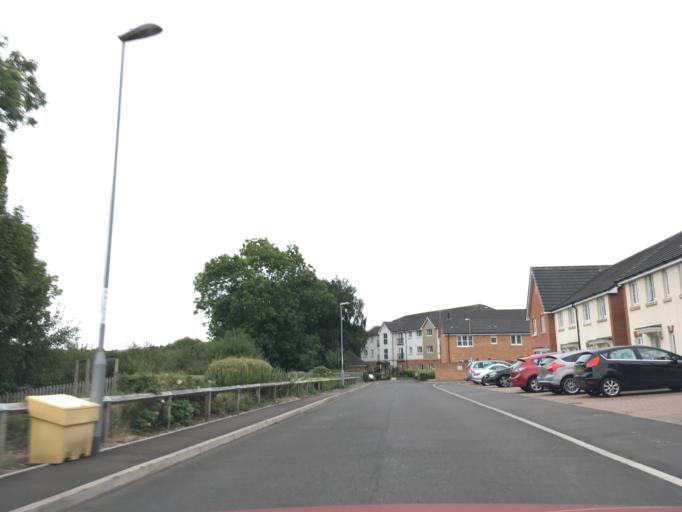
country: GB
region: Wales
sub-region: Newport
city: Newport
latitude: 51.5798
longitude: -3.0461
